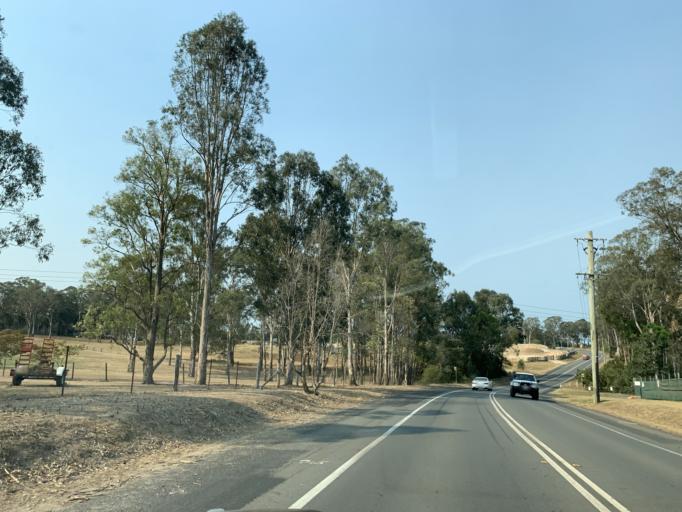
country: AU
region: New South Wales
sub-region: Blacktown
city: Rouse Hill
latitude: -33.6638
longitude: 150.9201
